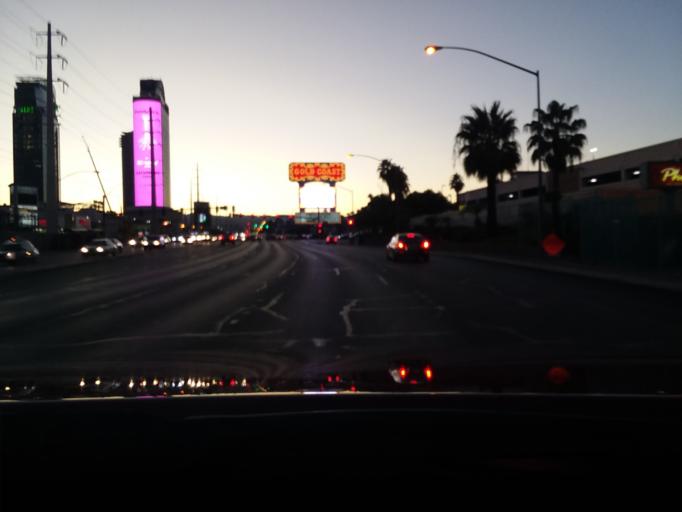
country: US
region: Nevada
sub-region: Clark County
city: Paradise
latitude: 36.1156
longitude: -115.1886
